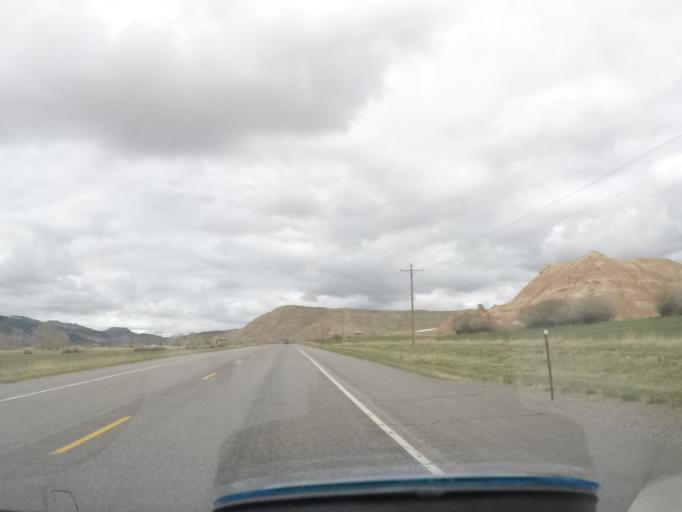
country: US
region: Wyoming
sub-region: Sublette County
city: Pinedale
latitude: 43.5626
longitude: -109.6993
